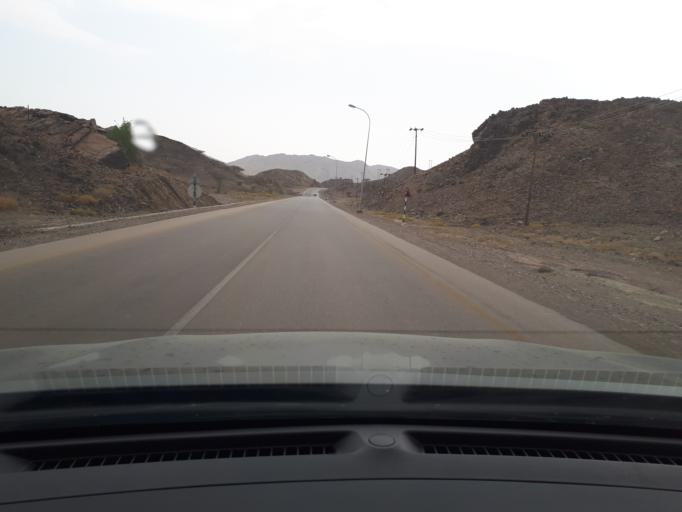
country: OM
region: Ash Sharqiyah
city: Badiyah
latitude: 22.5560
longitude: 59.0068
